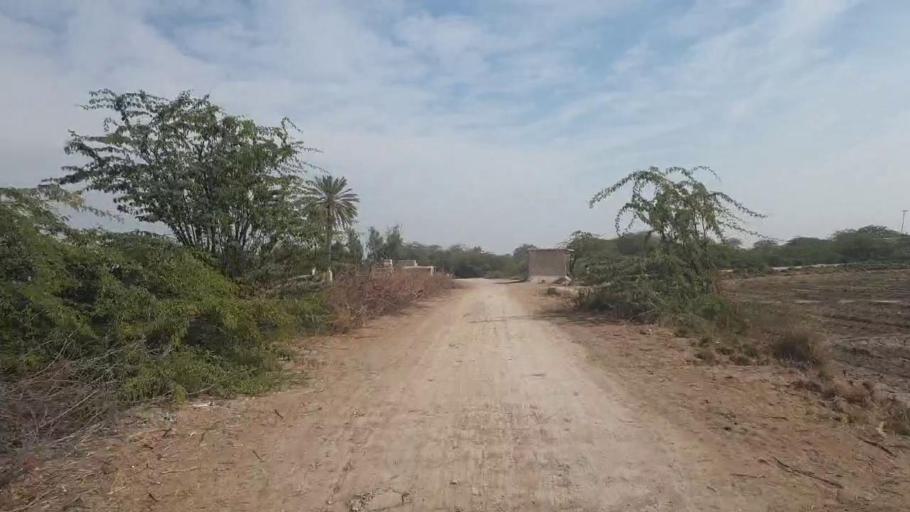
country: PK
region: Sindh
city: Nawabshah
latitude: 26.1138
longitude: 68.4938
